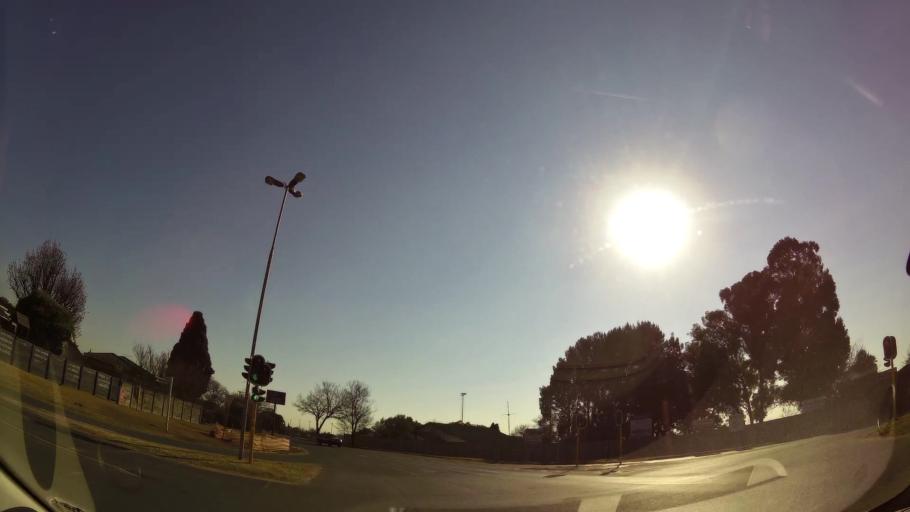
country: ZA
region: Gauteng
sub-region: Ekurhuleni Metropolitan Municipality
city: Benoni
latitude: -26.1588
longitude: 28.3167
